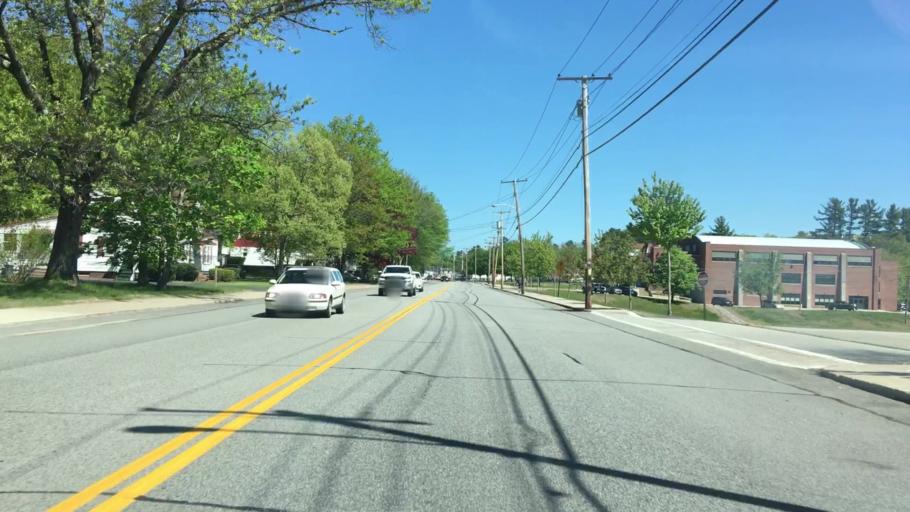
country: US
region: Maine
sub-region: York County
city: Sanford (historical)
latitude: 43.4502
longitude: -70.7876
